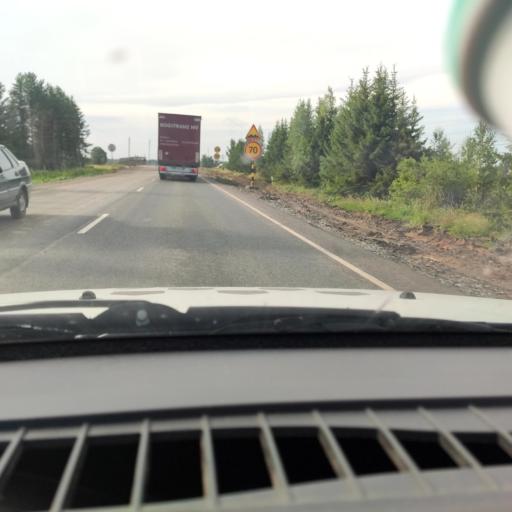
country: RU
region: Kirov
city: Kostino
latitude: 58.8339
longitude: 53.3058
